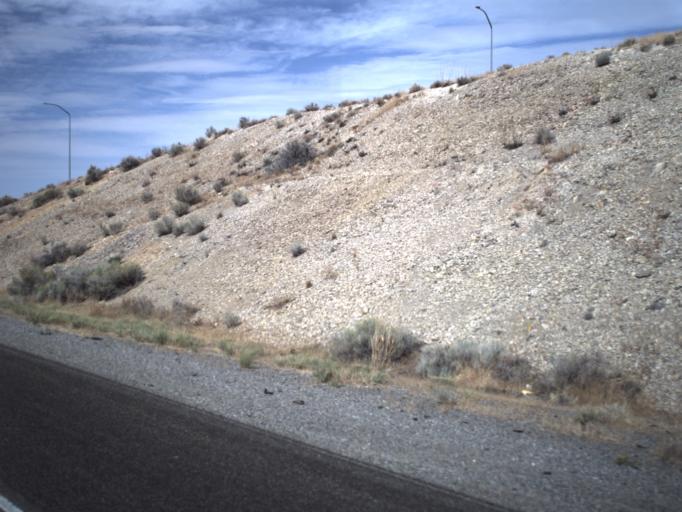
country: US
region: Utah
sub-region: Tooele County
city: Grantsville
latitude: 40.7607
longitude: -113.0108
